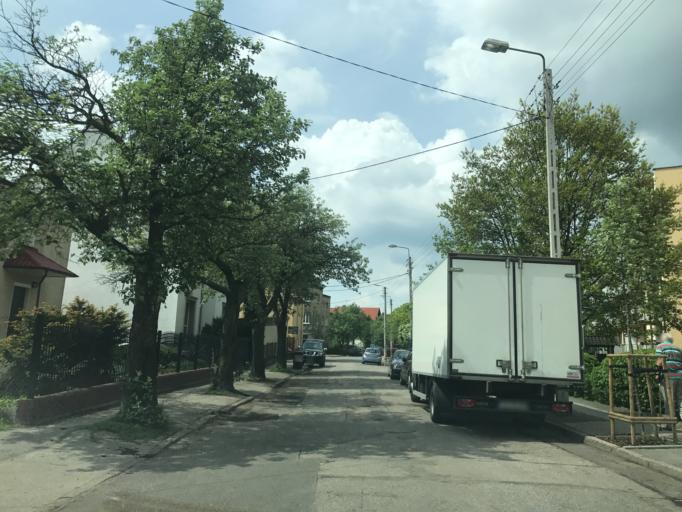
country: PL
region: Kujawsko-Pomorskie
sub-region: Bydgoszcz
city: Bydgoszcz
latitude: 53.1335
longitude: 18.0266
